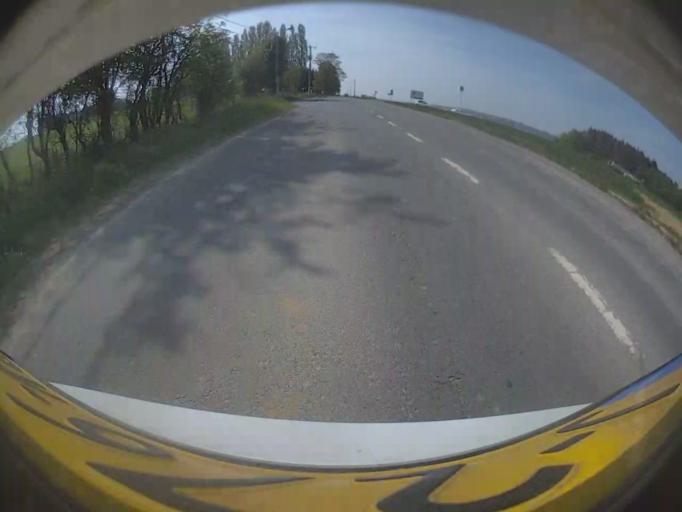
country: BE
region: Wallonia
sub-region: Province de Namur
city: Dinant
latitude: 50.2622
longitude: 4.9639
